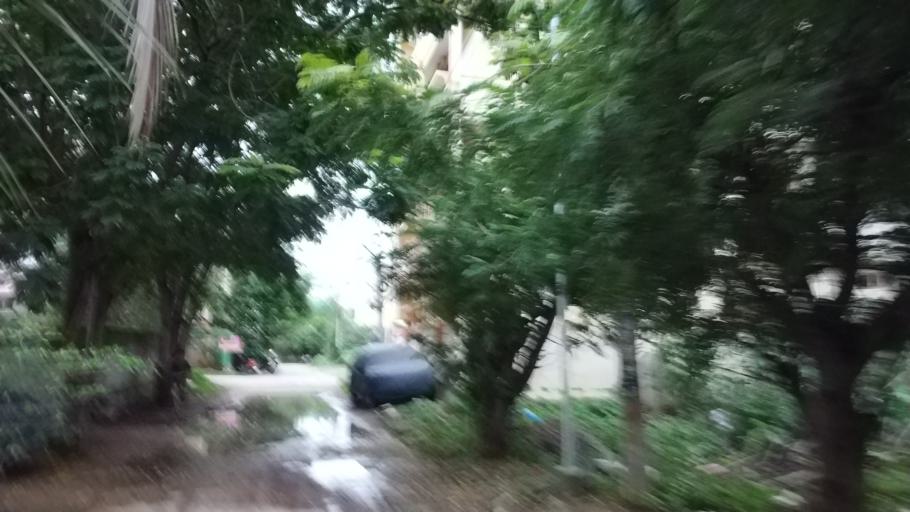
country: IN
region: Telangana
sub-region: Medak
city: Serilingampalle
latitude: 17.5096
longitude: 78.3066
